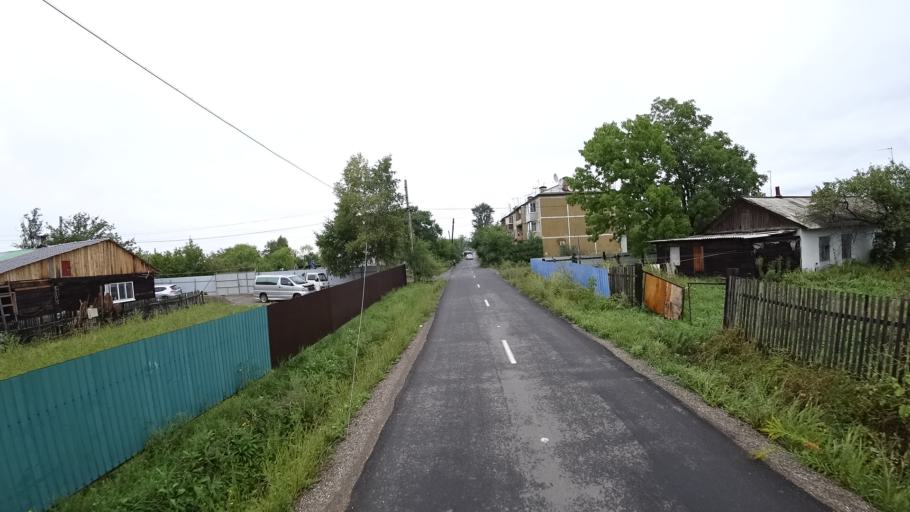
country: RU
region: Primorskiy
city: Monastyrishche
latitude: 44.1998
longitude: 132.4964
